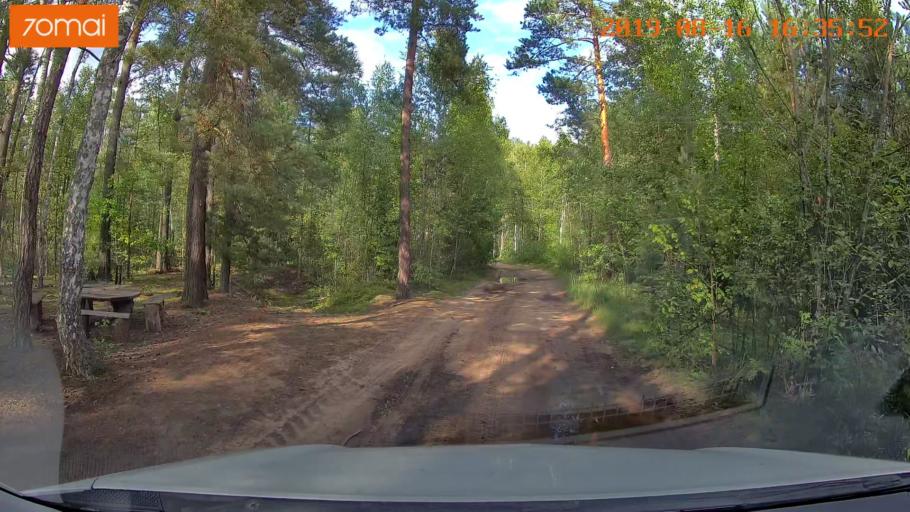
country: BY
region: Mogilev
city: Asipovichy
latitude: 53.2309
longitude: 28.7755
